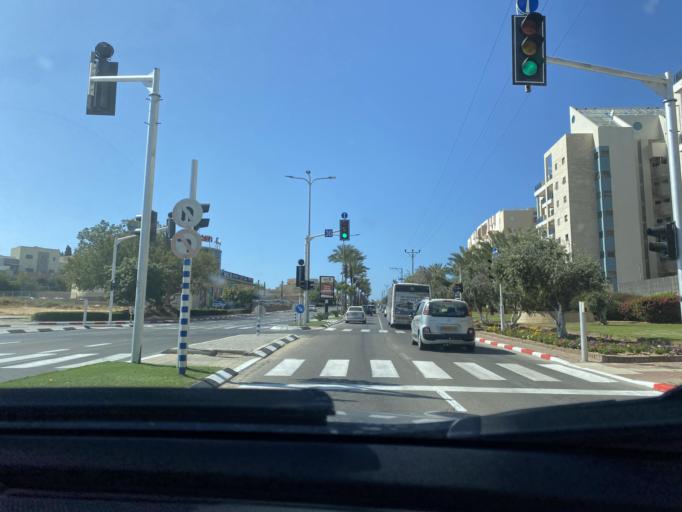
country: IL
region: Southern District
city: Ashqelon
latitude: 31.6768
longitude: 34.5766
